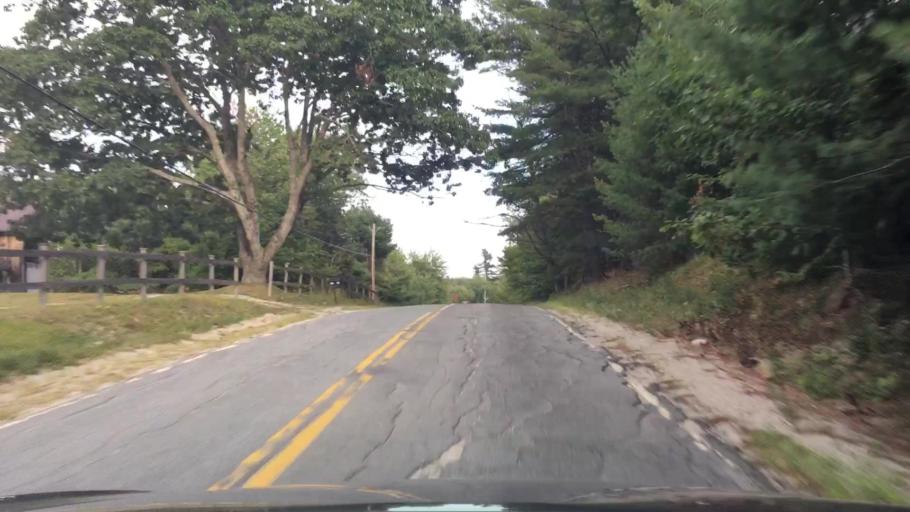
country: US
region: Maine
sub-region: Hancock County
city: Surry
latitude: 44.5003
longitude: -68.5670
